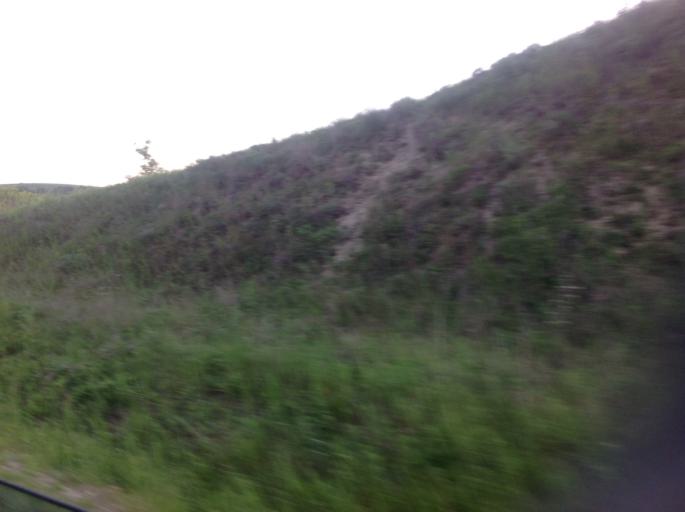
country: HU
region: Komarom-Esztergom
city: Csolnok
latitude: 47.6524
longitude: 18.7141
